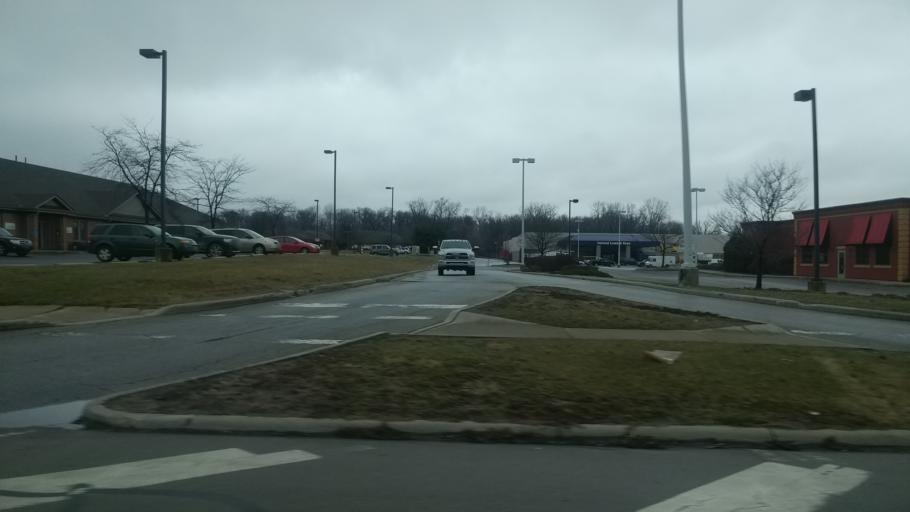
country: US
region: Ohio
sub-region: Lucas County
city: Sylvania
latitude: 41.6738
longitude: -83.7126
